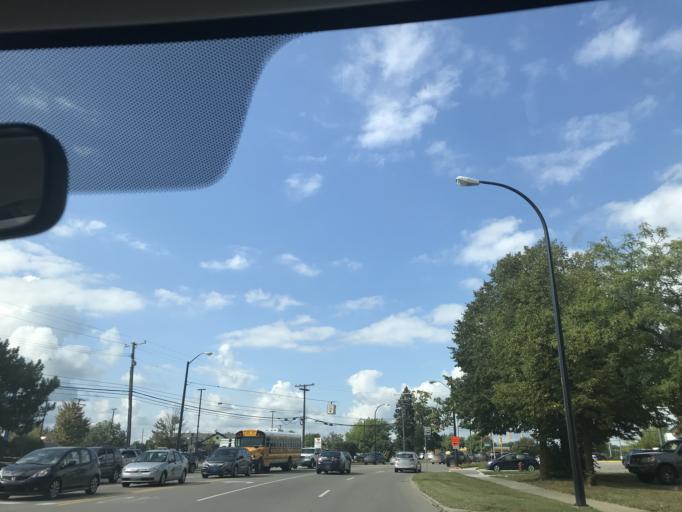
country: US
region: Michigan
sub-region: Washtenaw County
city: Ann Arbor
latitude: 42.2791
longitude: -83.7799
